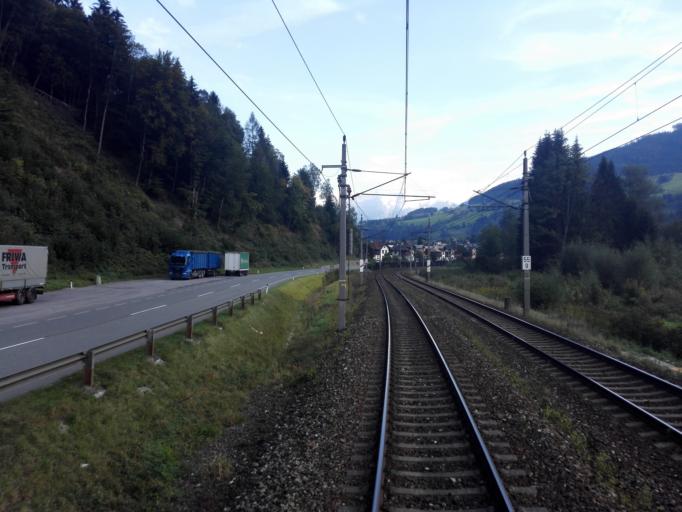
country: AT
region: Salzburg
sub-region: Politischer Bezirk Sankt Johann im Pongau
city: Bischofshofen
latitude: 47.3919
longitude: 13.2161
